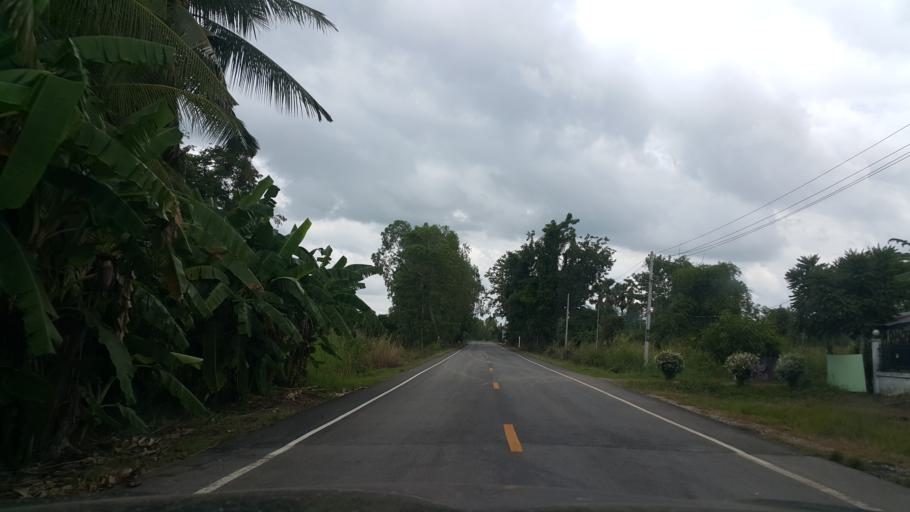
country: TH
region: Sukhothai
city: Kong Krailat
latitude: 16.9217
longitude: 99.8883
